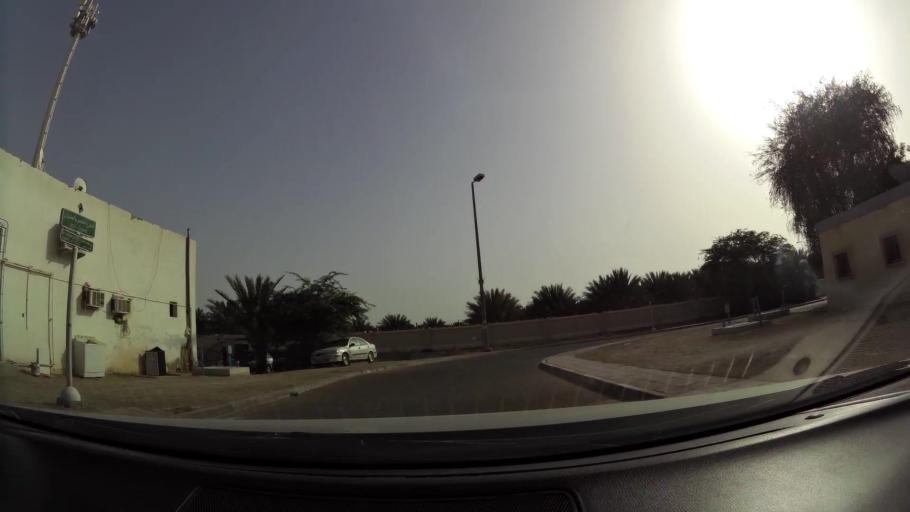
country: AE
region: Abu Dhabi
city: Al Ain
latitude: 24.1381
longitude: 55.6899
